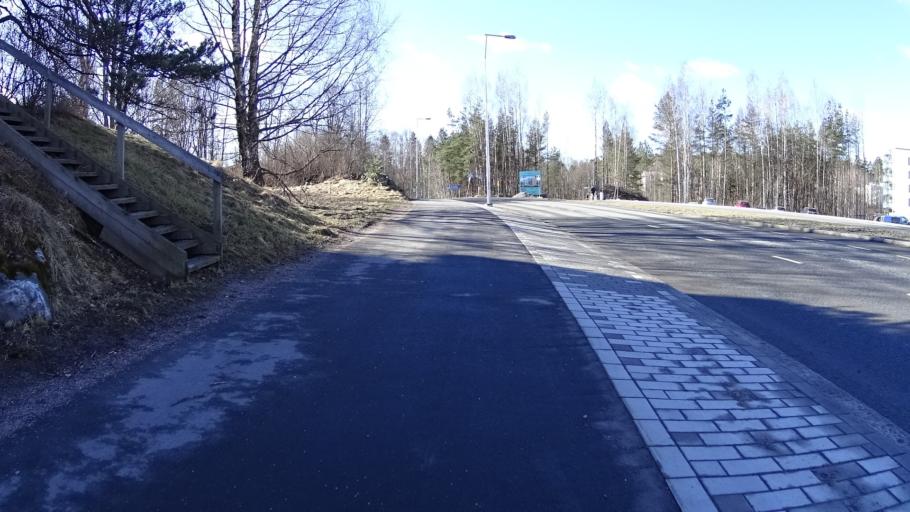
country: FI
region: Uusimaa
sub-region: Helsinki
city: Teekkarikylae
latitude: 60.2542
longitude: 24.8692
